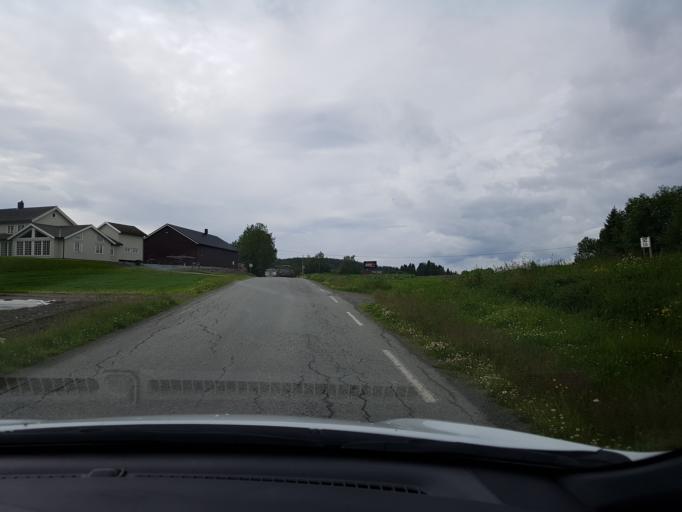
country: NO
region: Nord-Trondelag
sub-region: Frosta
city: Frosta
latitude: 63.6285
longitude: 10.7678
